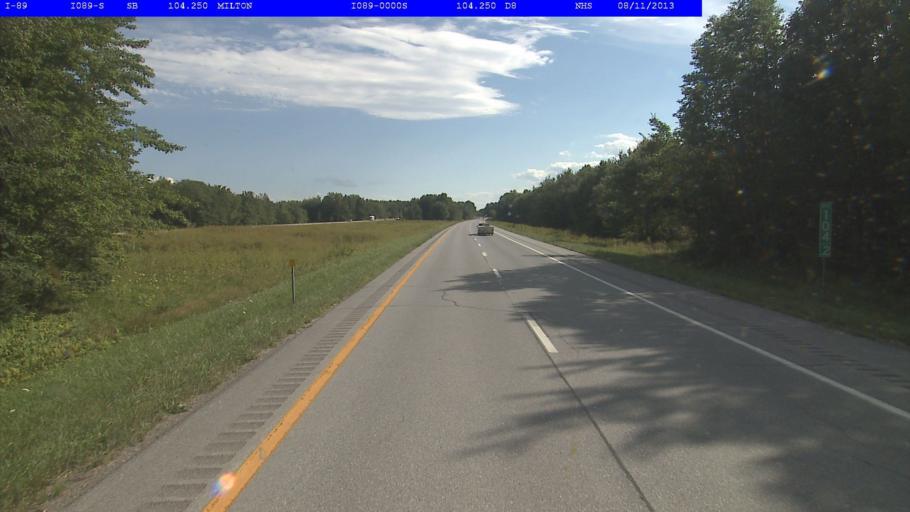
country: US
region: Vermont
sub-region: Chittenden County
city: Milton
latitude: 44.6739
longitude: -73.1321
